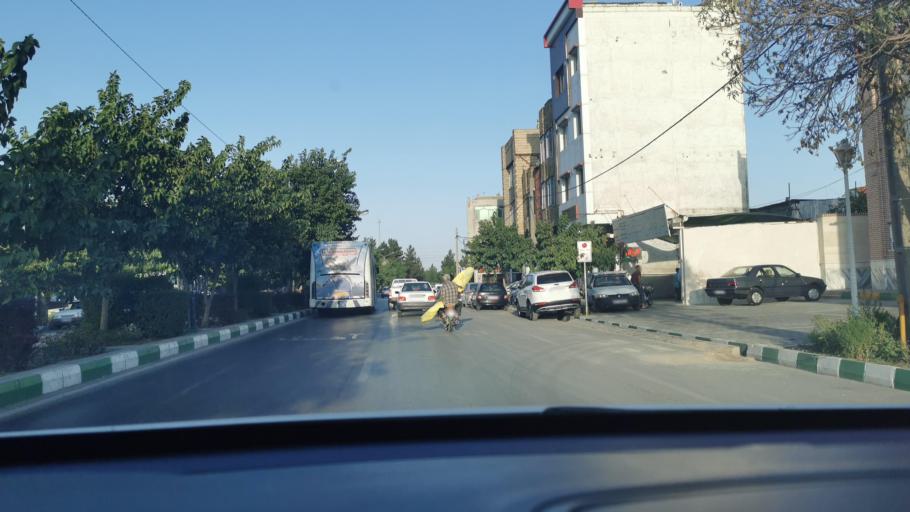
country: IR
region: Razavi Khorasan
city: Mashhad
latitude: 36.2887
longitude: 59.6561
